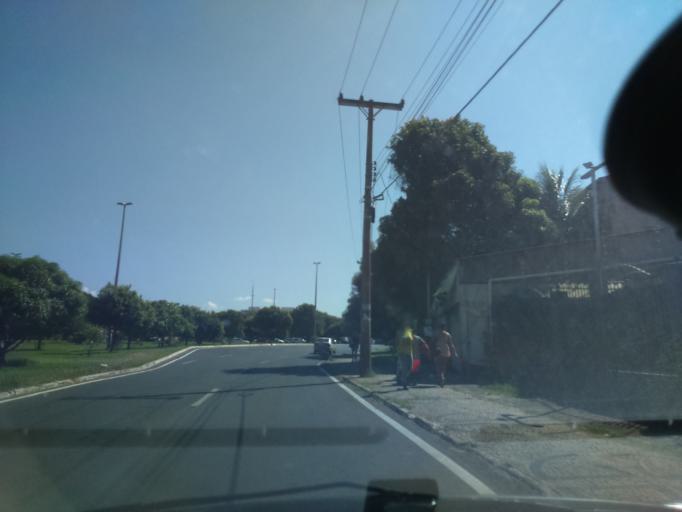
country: BR
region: Federal District
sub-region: Brasilia
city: Brasilia
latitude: -15.8479
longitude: -47.9751
